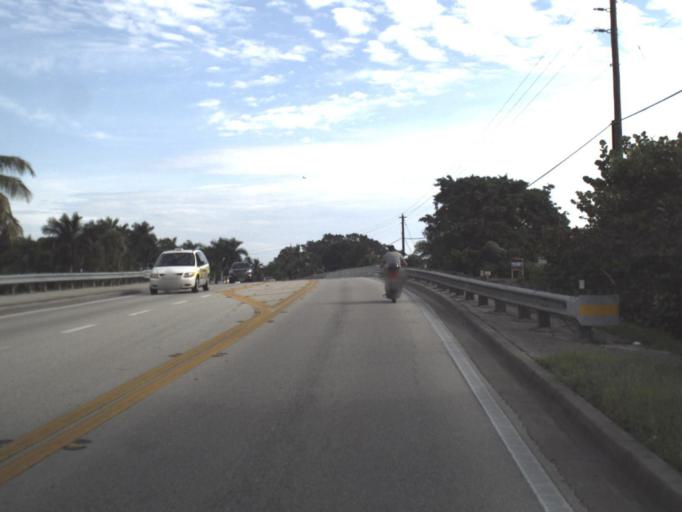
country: US
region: Florida
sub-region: Lee County
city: Whiskey Creek
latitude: 26.5760
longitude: -81.8984
